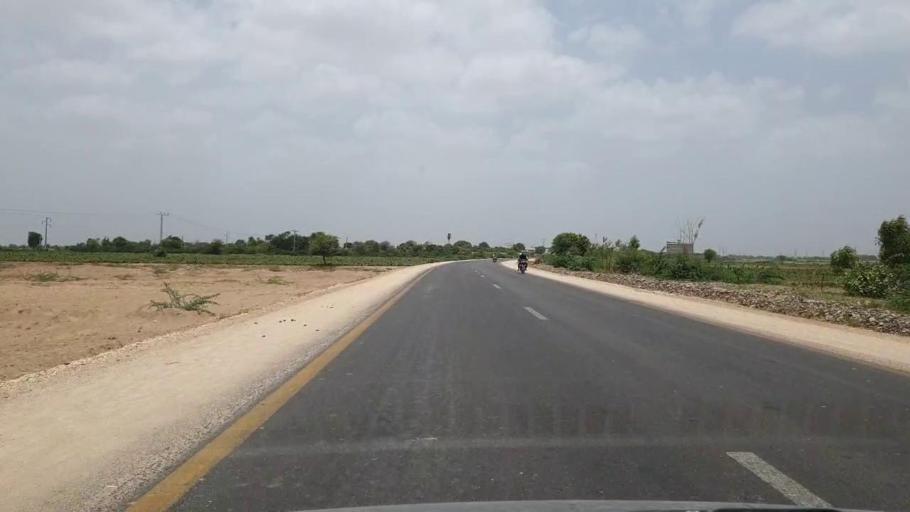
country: PK
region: Sindh
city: Naukot
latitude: 24.8433
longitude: 69.4300
